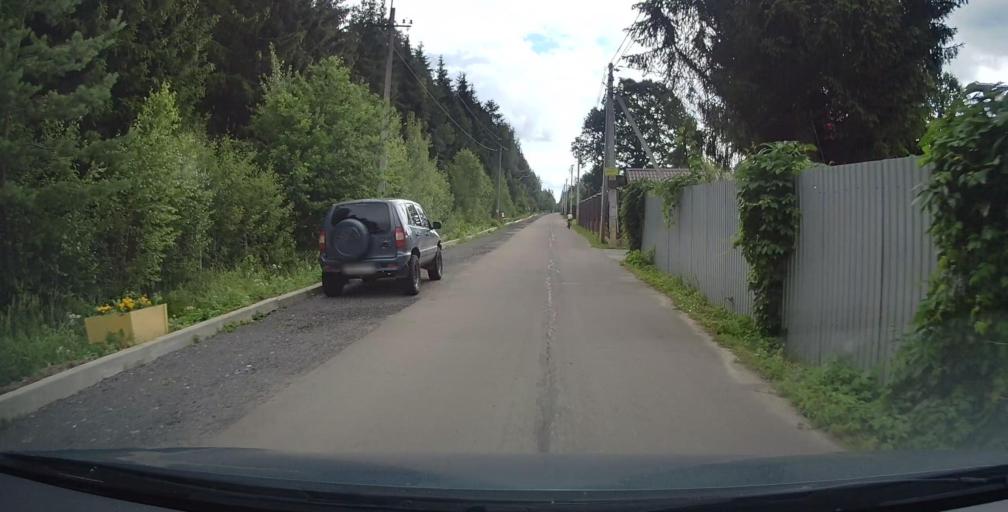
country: RU
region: Moskovskaya
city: Selyatino
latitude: 55.3947
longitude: 37.0132
